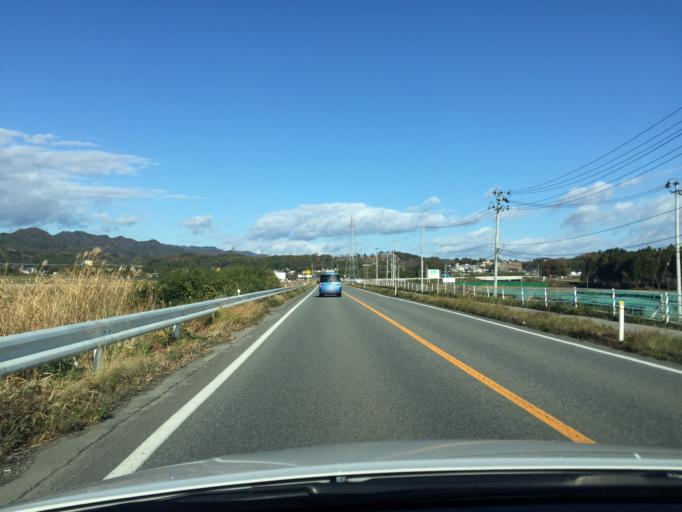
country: JP
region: Fukushima
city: Namie
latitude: 37.2704
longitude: 140.9939
